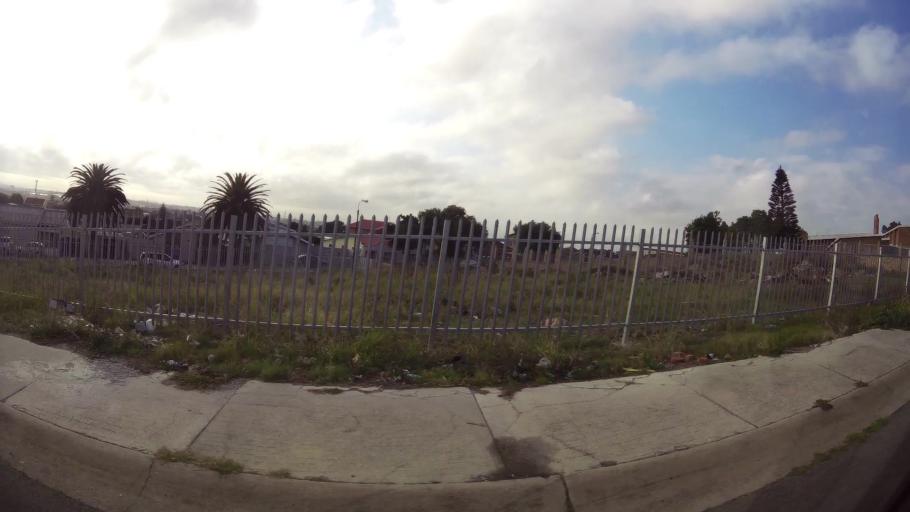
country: ZA
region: Eastern Cape
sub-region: Nelson Mandela Bay Metropolitan Municipality
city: Port Elizabeth
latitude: -33.9229
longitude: 25.5548
